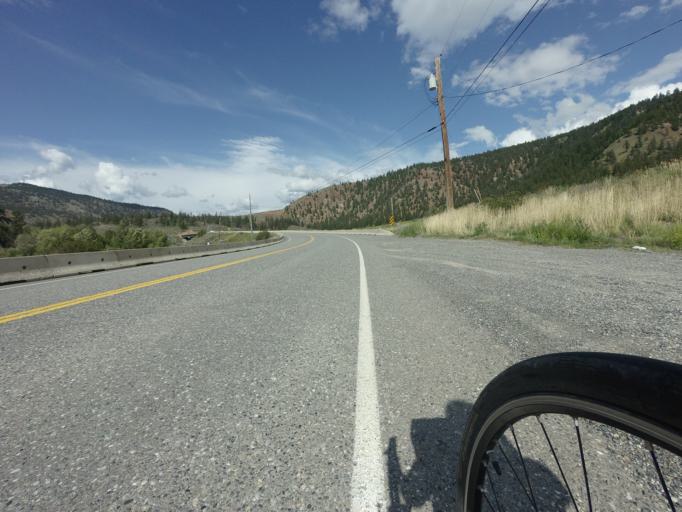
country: CA
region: British Columbia
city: Lillooet
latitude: 50.8699
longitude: -121.8333
